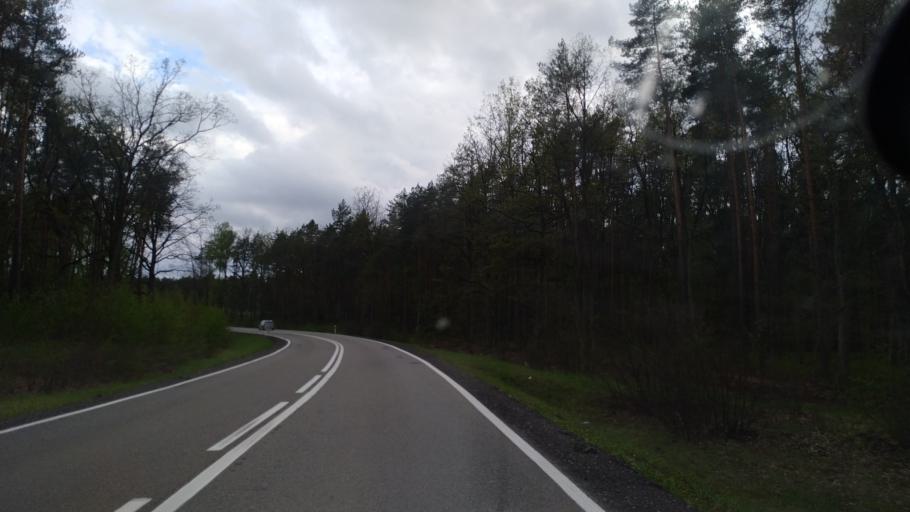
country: PL
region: Pomeranian Voivodeship
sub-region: Powiat kwidzynski
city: Ryjewo
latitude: 53.8346
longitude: 18.9921
